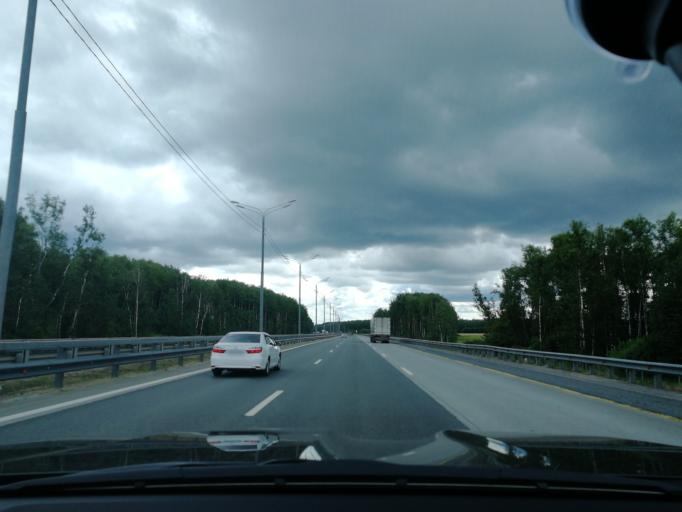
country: RU
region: Moskovskaya
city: Barybino
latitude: 55.2233
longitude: 37.8741
